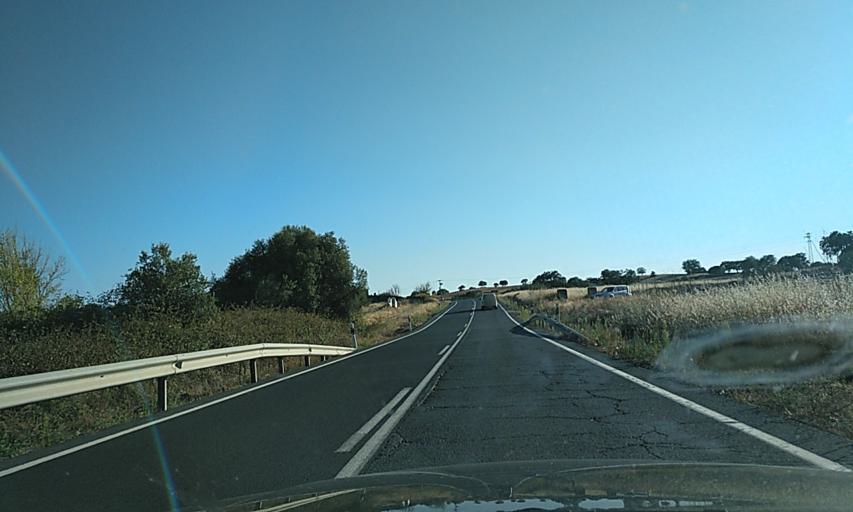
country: ES
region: Andalusia
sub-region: Provincia de Huelva
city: Alosno
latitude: 37.5438
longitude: -7.1264
